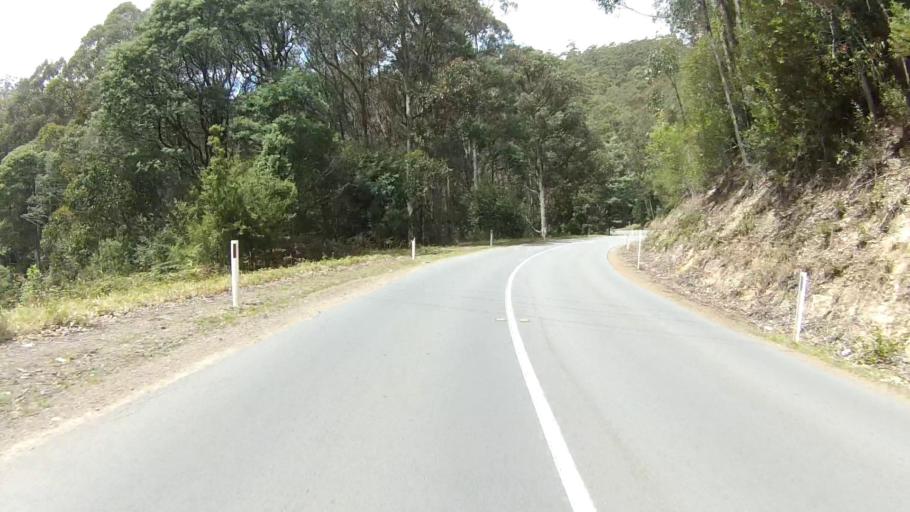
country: AU
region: Tasmania
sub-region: Kingborough
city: Kettering
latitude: -43.1279
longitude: 147.1664
